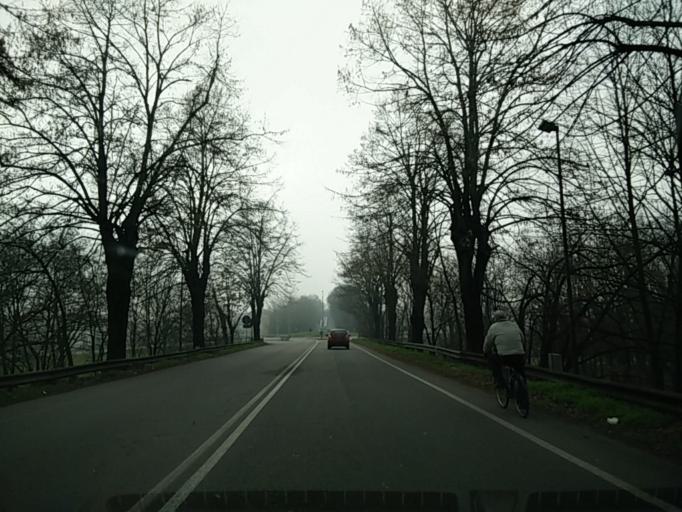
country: IT
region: Lombardy
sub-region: Provincia di Pavia
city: Rotta
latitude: 45.1783
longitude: 9.1464
